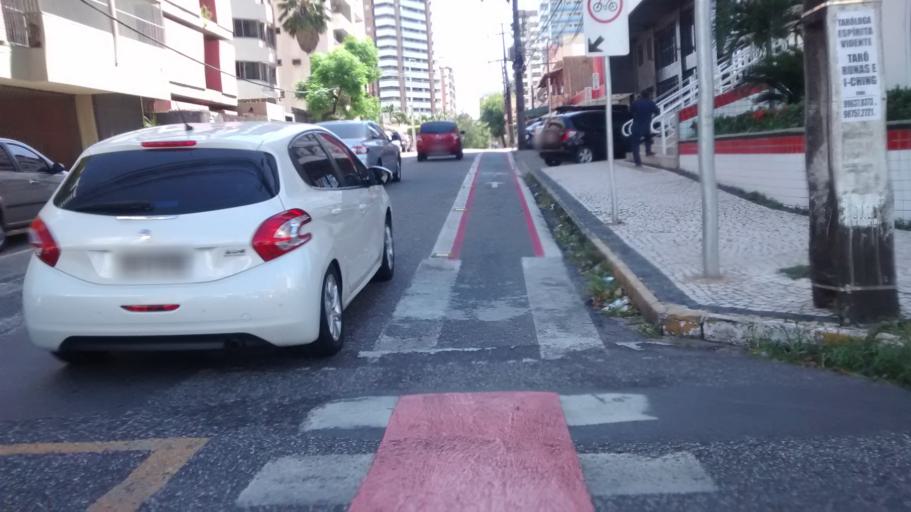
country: BR
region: Ceara
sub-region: Fortaleza
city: Fortaleza
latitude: -3.7431
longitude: -38.5005
